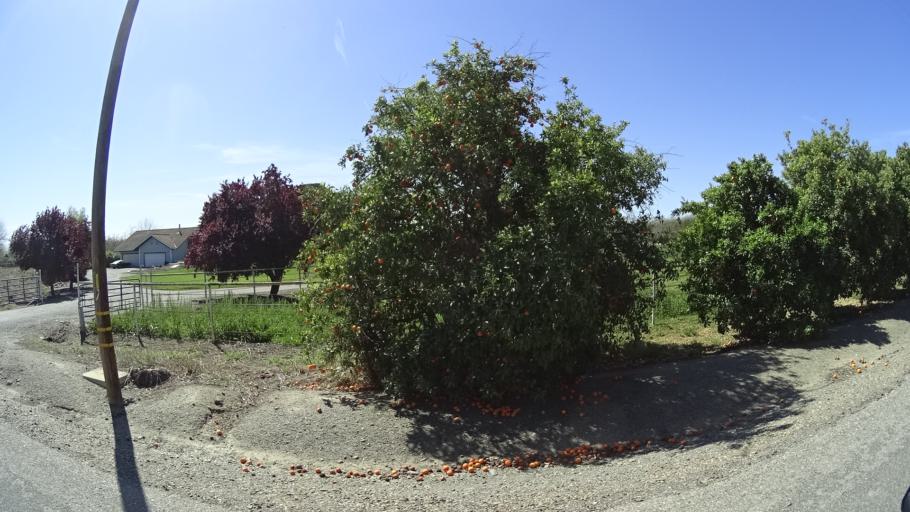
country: US
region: California
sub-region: Glenn County
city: Orland
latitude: 39.7432
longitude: -122.1311
